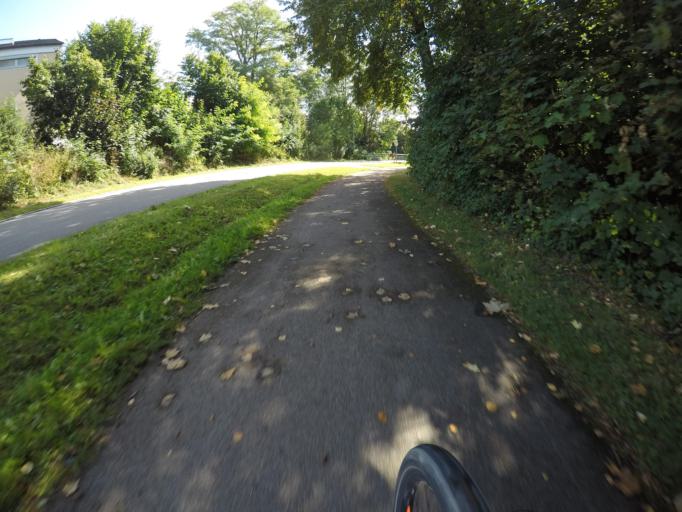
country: DE
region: Bavaria
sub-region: Swabia
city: Hochstadt an der Donau
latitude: 48.6195
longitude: 10.5759
